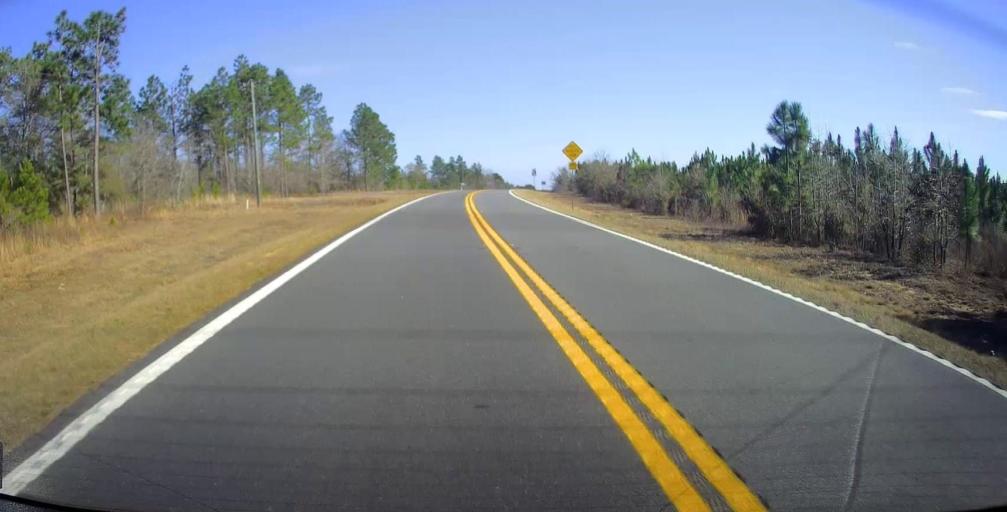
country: US
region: Georgia
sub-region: Taylor County
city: Butler
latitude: 32.4389
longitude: -84.2565
